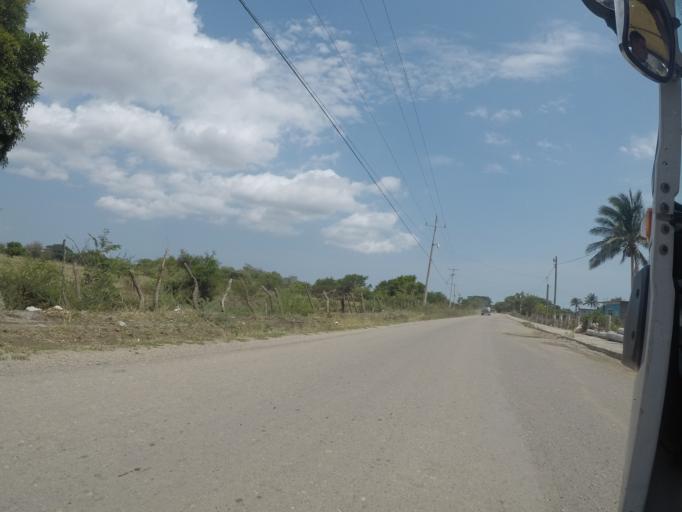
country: MX
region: Oaxaca
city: Union Hidalgo
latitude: 16.4611
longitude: -94.8295
